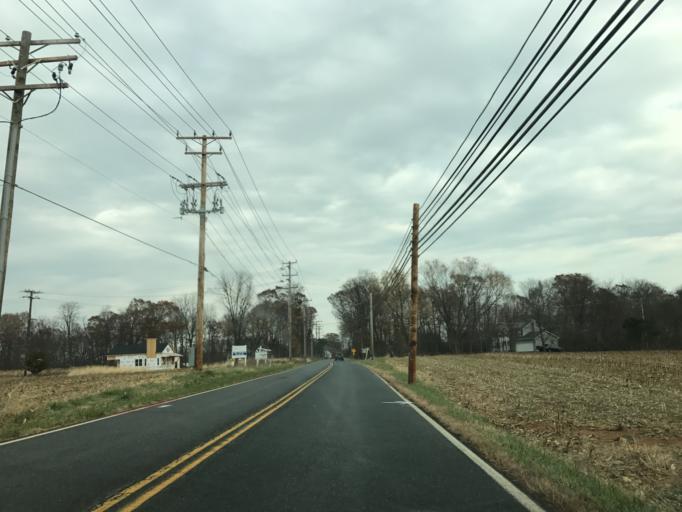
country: US
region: Maryland
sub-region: Harford County
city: Jarrettsville
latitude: 39.6083
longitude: -76.4622
